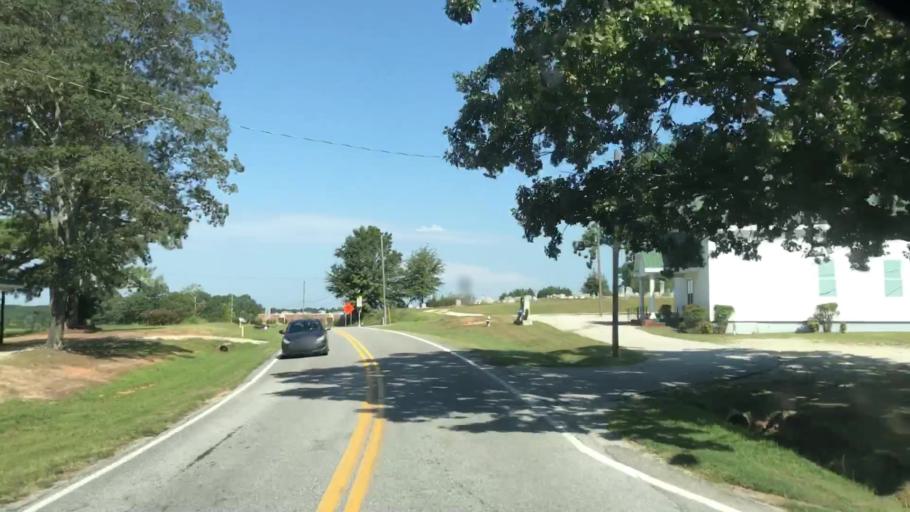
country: US
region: Georgia
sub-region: Walton County
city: Loganville
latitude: 33.8508
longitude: -83.8607
